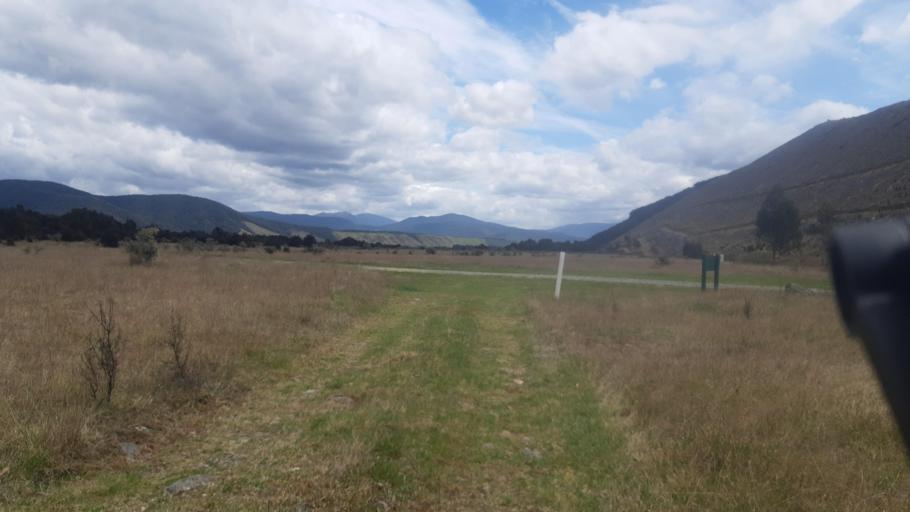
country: NZ
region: Tasman
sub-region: Tasman District
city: Wakefield
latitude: -41.7696
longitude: 172.7972
